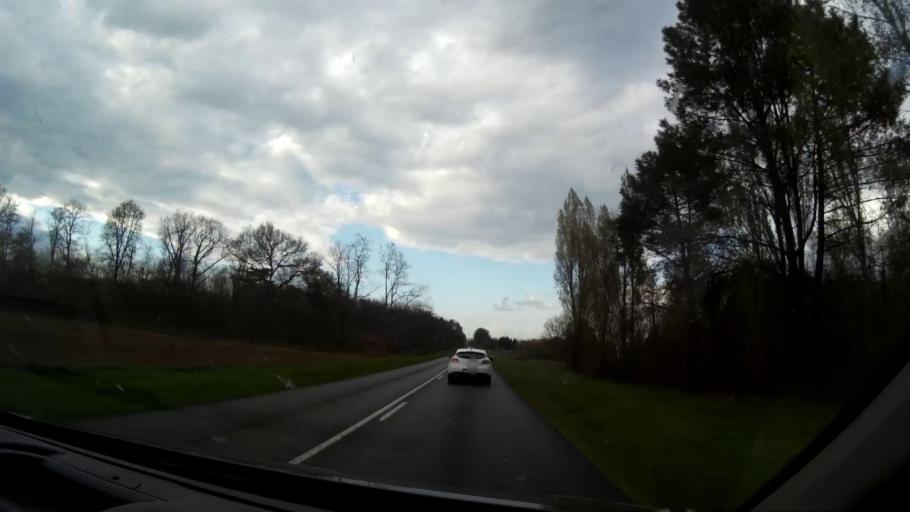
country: FR
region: Centre
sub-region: Departement du Loir-et-Cher
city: Cormeray
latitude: 47.4616
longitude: 1.4251
